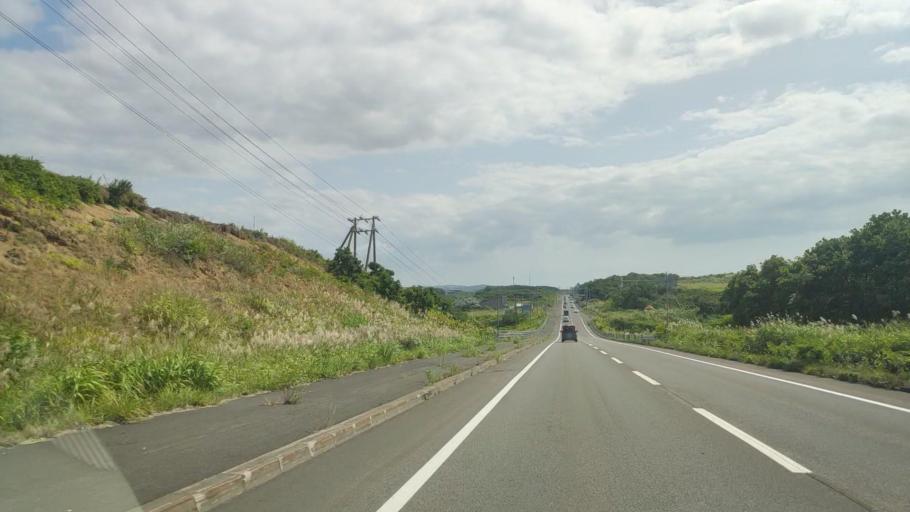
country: JP
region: Hokkaido
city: Rumoi
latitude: 44.2985
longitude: 141.6532
